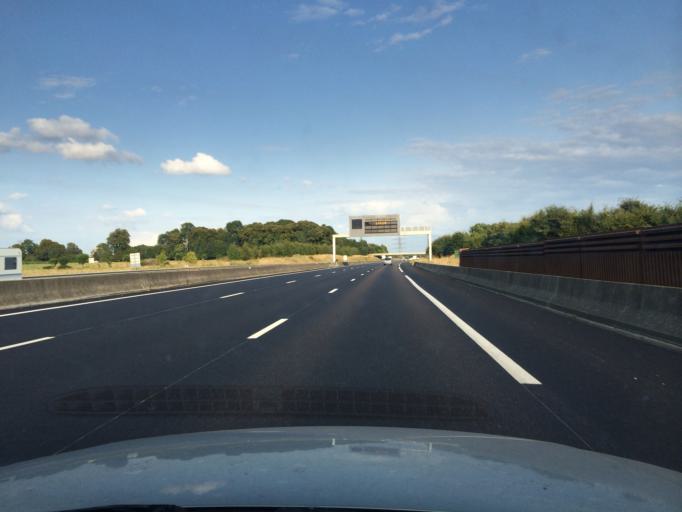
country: FR
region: Haute-Normandie
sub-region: Departement de l'Eure
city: Saint-Ouen-de-Thouberville
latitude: 49.3491
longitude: 0.9013
